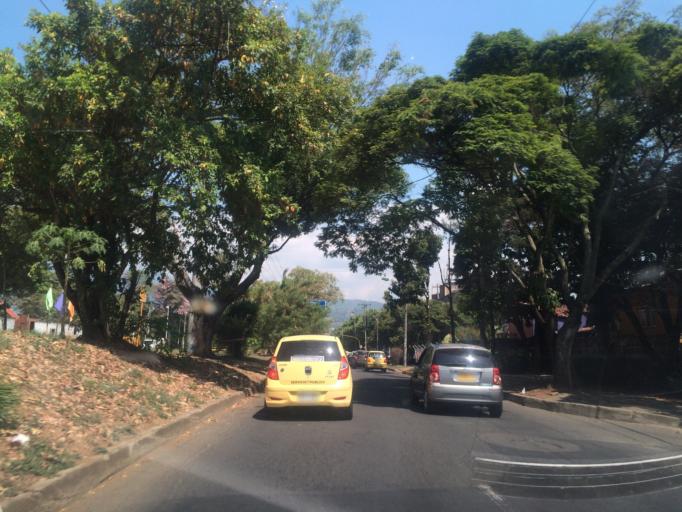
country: CO
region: Valle del Cauca
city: Cali
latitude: 3.4072
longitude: -76.5290
